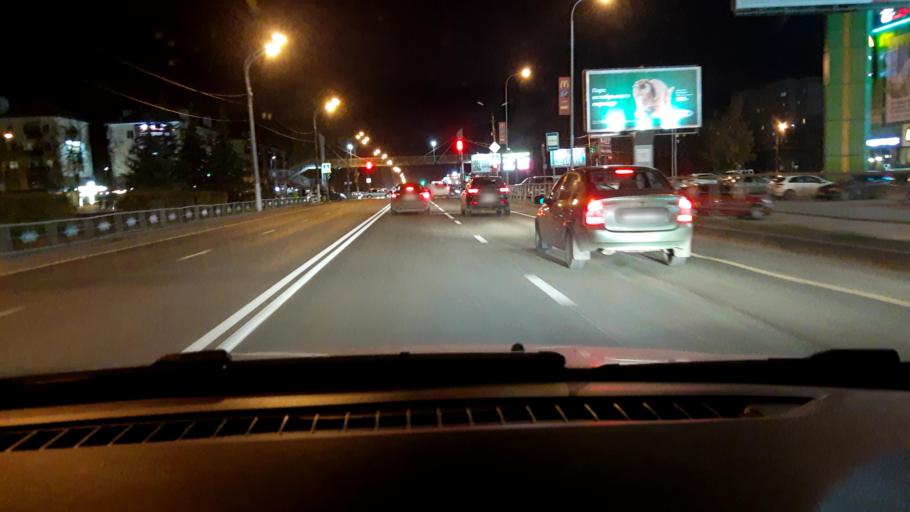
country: RU
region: Nizjnij Novgorod
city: Kstovo
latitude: 56.1511
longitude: 44.2082
